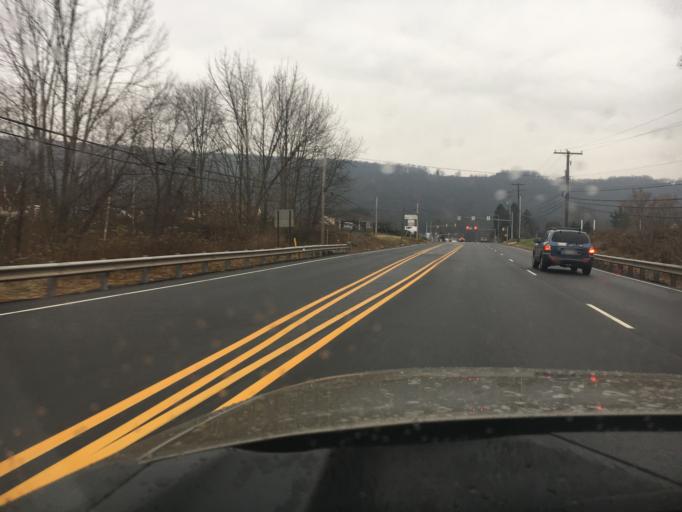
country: US
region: Pennsylvania
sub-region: Luzerne County
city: Harleigh
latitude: 41.0129
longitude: -75.9655
